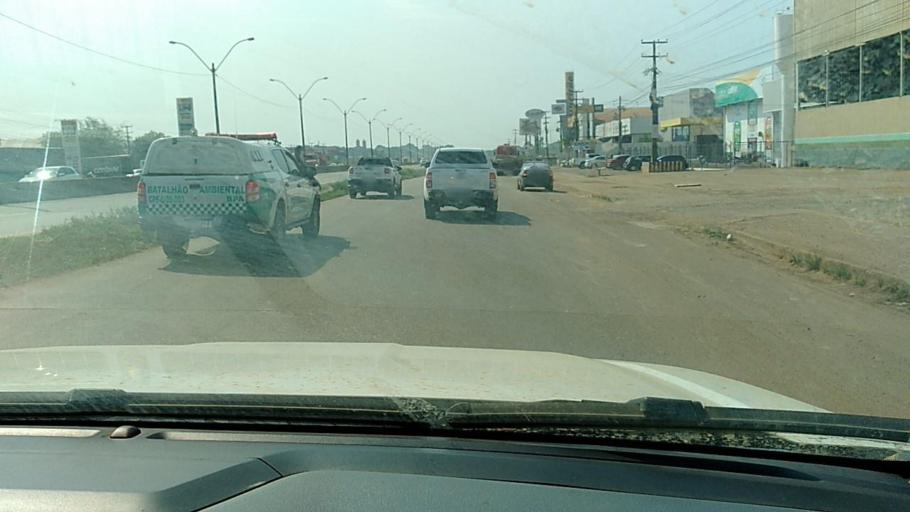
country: BR
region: Rondonia
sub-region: Porto Velho
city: Porto Velho
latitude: -8.7895
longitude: -63.8521
